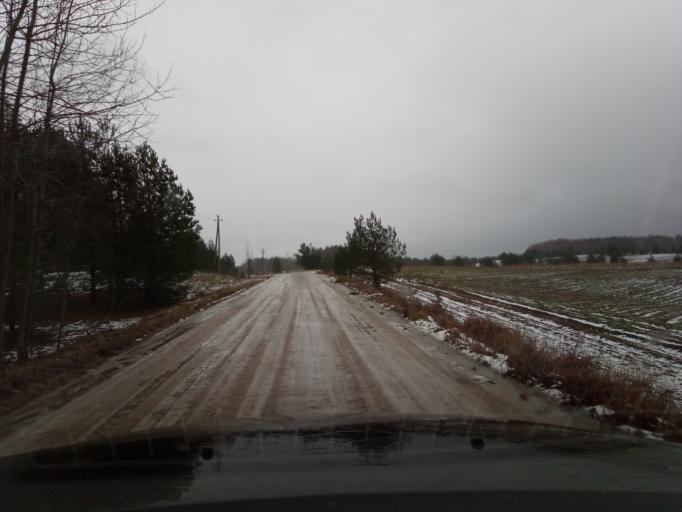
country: LT
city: Svencioneliai
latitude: 55.3440
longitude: 25.8395
